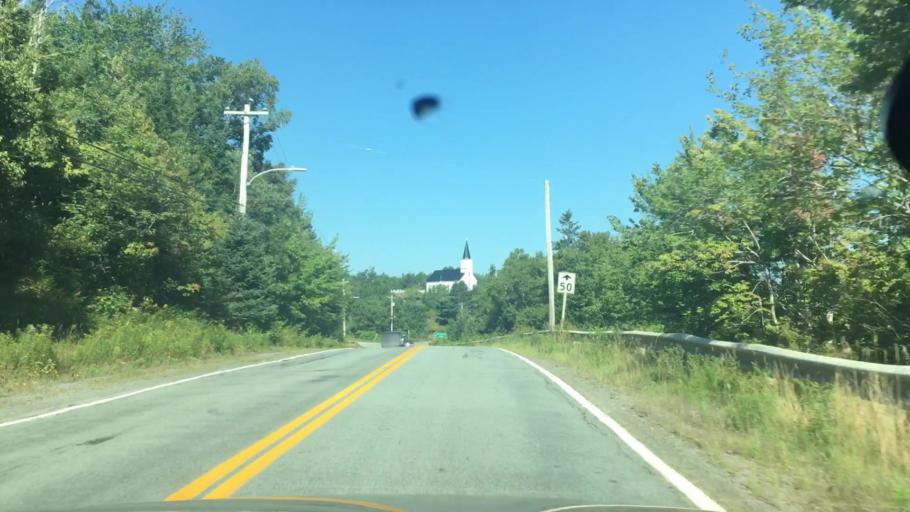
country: CA
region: Nova Scotia
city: New Glasgow
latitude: 44.9209
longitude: -62.5441
